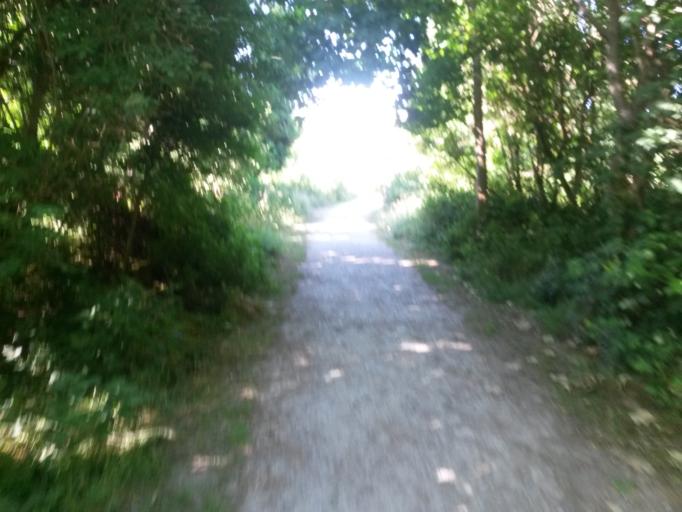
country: IE
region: Leinster
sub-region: Wicklow
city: Blessington
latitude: 53.1560
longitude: -6.5374
